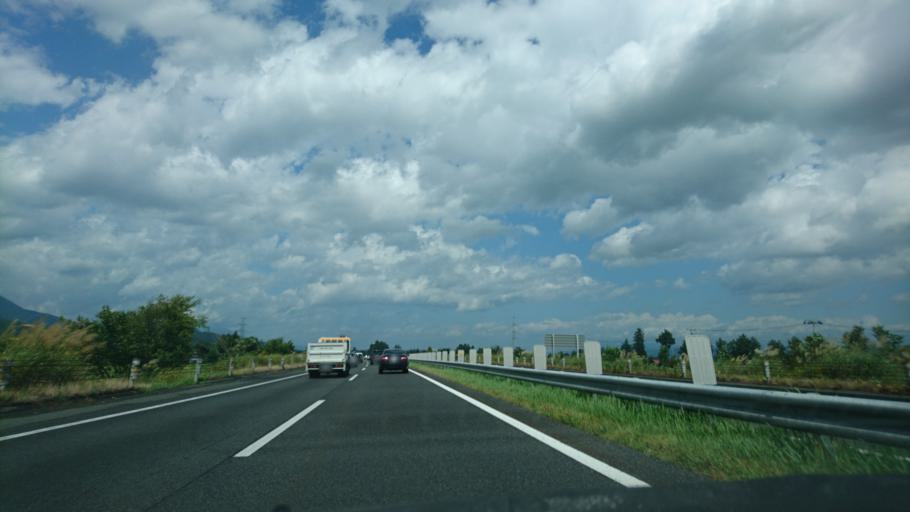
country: JP
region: Iwate
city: Morioka-shi
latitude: 39.5743
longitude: 141.1207
